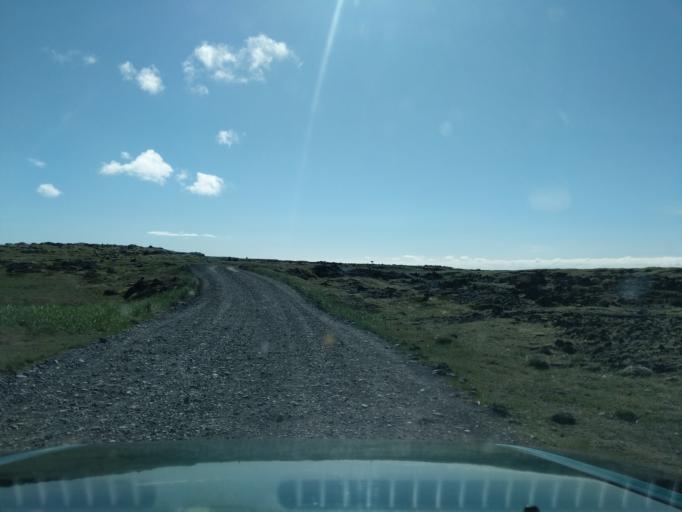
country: IS
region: West
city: Olafsvik
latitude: 64.8741
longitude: -24.0049
